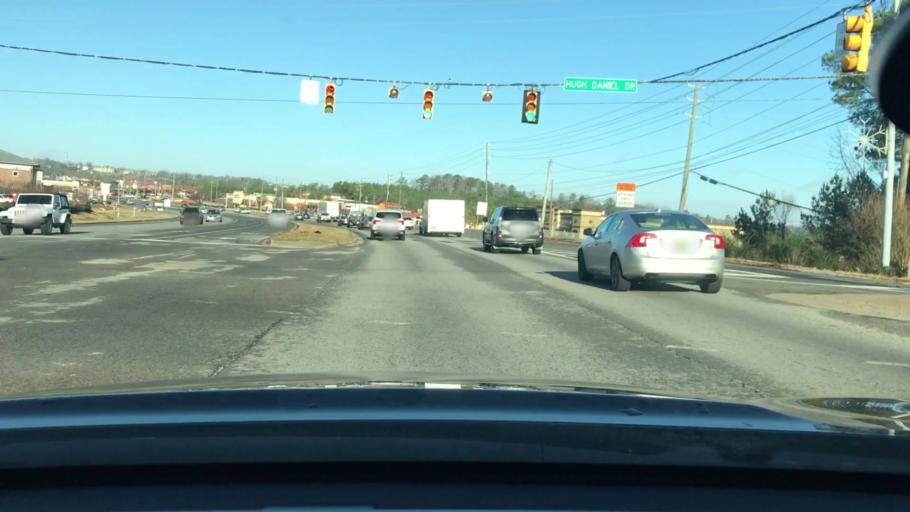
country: US
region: Alabama
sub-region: Shelby County
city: Lake Purdy
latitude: 33.4165
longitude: -86.6670
